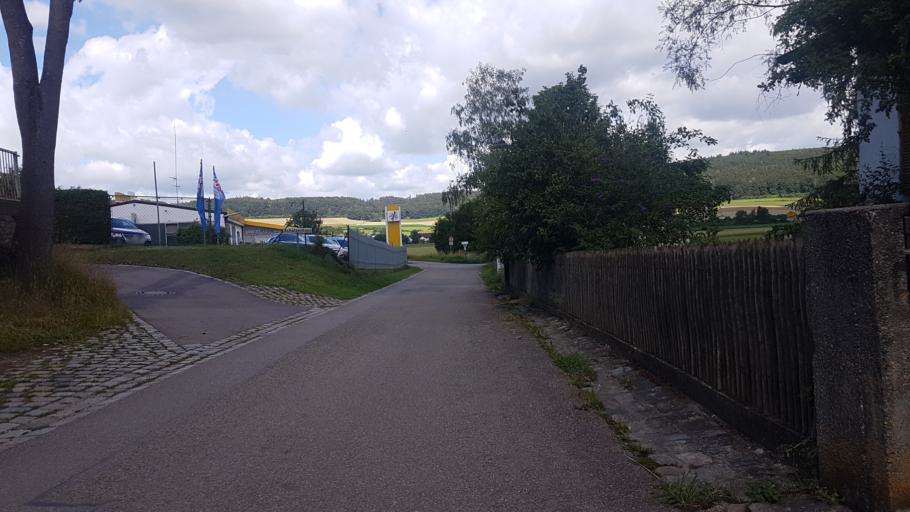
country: DE
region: Bavaria
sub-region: Upper Bavaria
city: Walting
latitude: 48.9341
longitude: 11.3239
